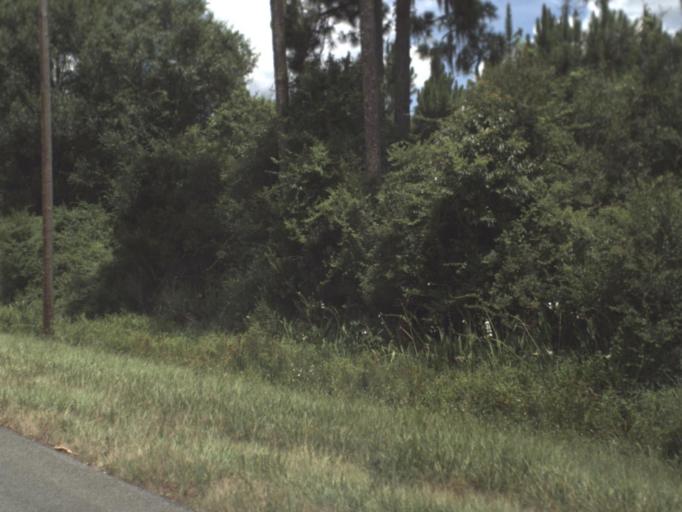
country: US
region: Florida
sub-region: Taylor County
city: Perry
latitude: 30.0894
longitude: -83.6760
